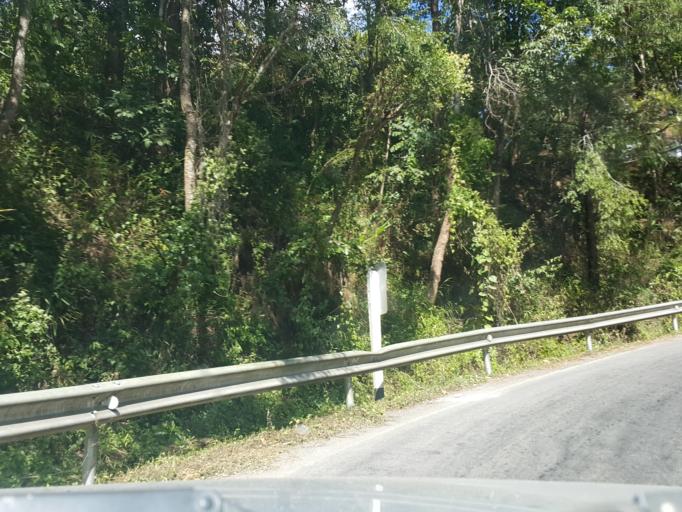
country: TH
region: Mae Hong Son
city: Mae Hi
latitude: 19.2311
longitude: 98.6675
